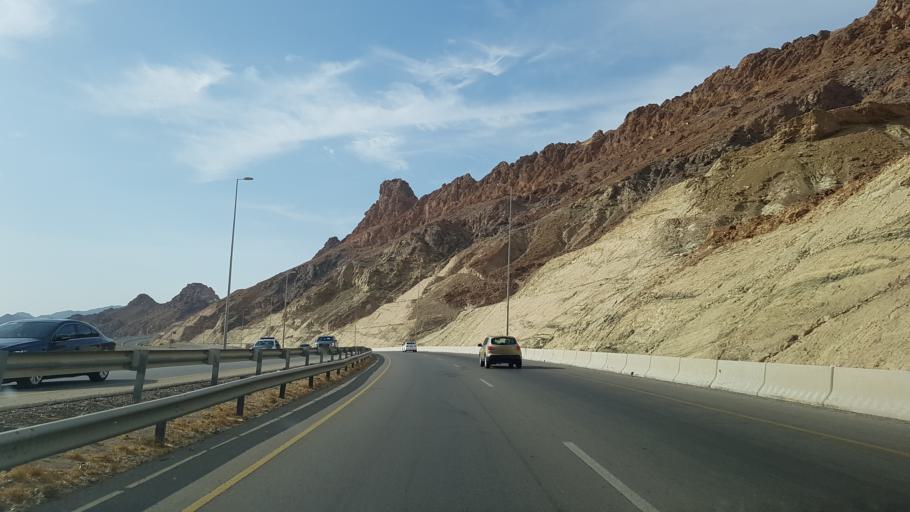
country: OM
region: Muhafazat ad Dakhiliyah
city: Bidbid
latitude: 23.4502
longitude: 58.1227
